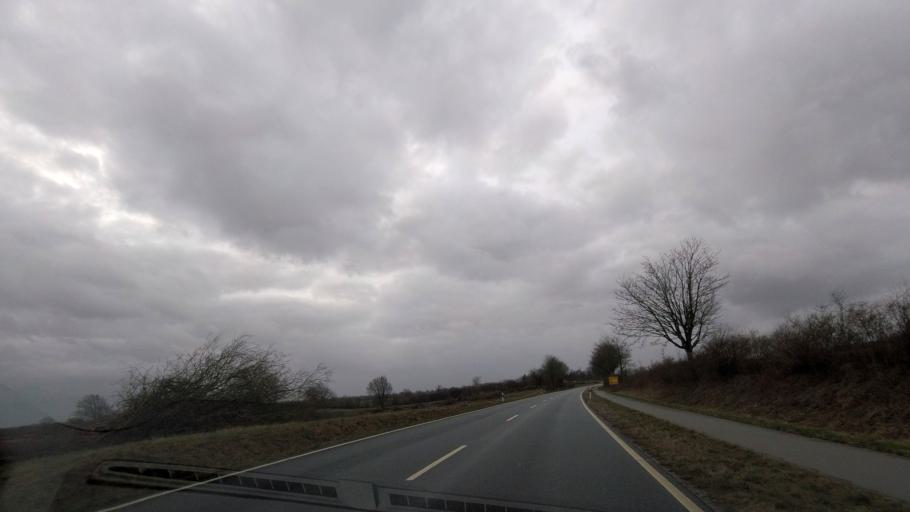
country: DE
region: Schleswig-Holstein
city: Schaalby
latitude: 54.5650
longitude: 9.6404
